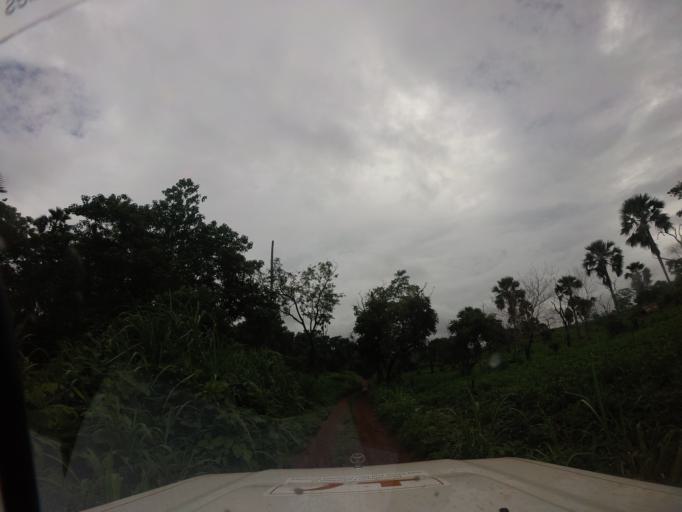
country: SL
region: Northern Province
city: Kamakwie
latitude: 9.6467
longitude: -12.2155
